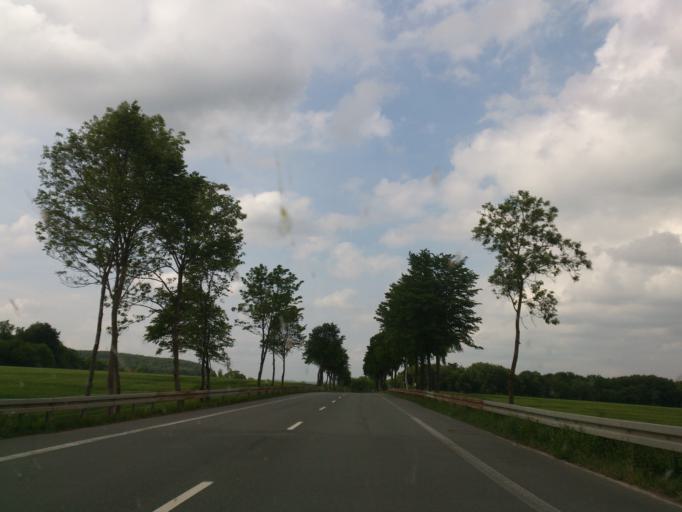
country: DE
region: North Rhine-Westphalia
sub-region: Regierungsbezirk Detmold
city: Willebadessen
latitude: 51.5972
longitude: 9.0329
